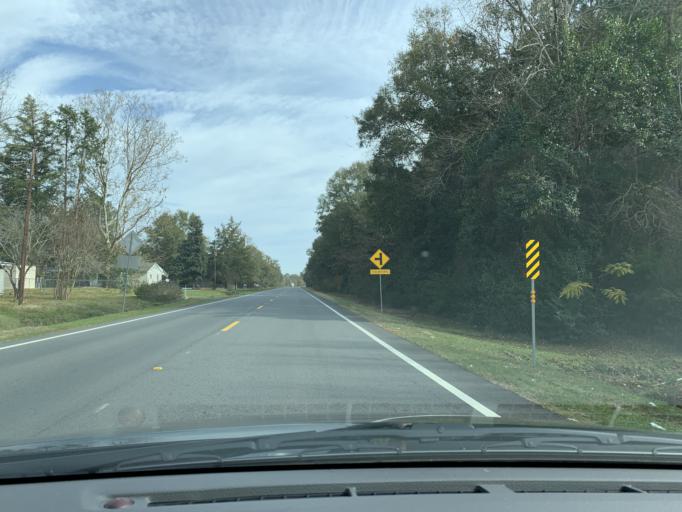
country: US
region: Georgia
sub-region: Wilcox County
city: Rochelle
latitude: 31.9594
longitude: -83.5999
